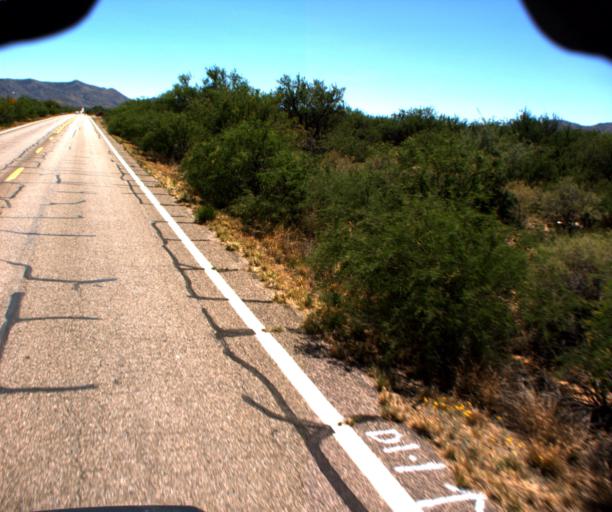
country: US
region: Arizona
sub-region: Pima County
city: Vail
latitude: 31.9655
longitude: -110.6730
